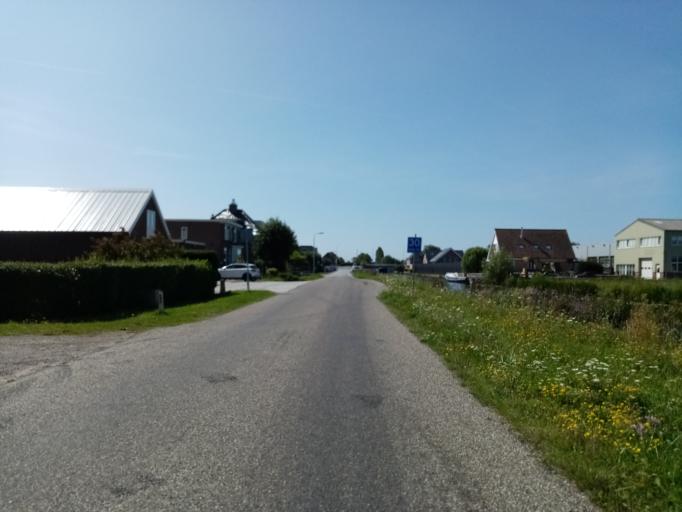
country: NL
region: South Holland
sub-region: Gemeente Hillegom
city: Hillegom
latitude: 52.2998
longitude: 4.5561
